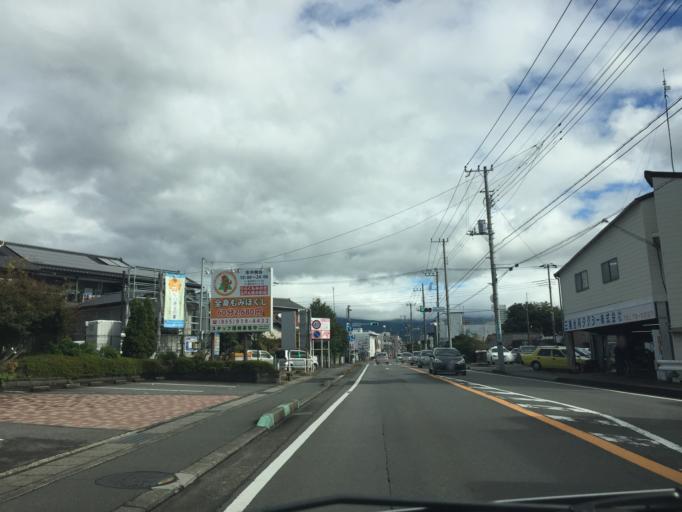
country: JP
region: Shizuoka
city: Mishima
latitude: 35.1165
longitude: 138.9033
